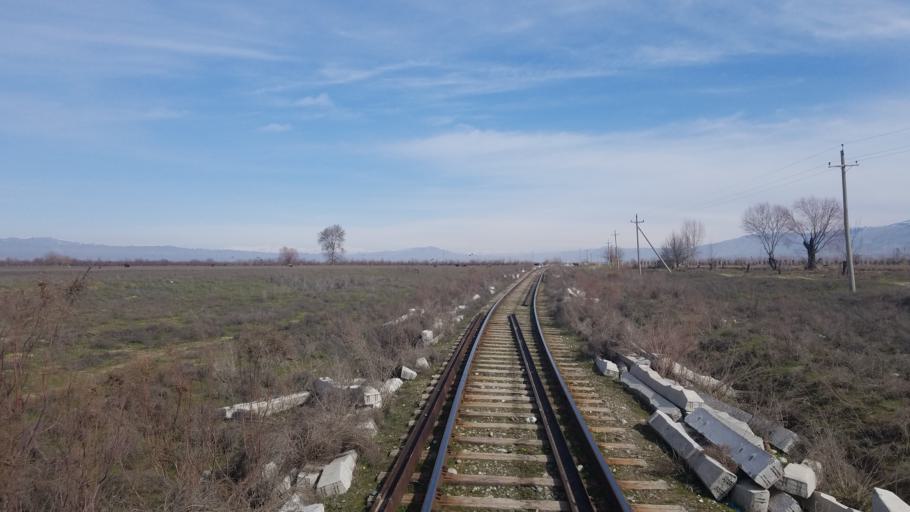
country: TJ
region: Khatlon
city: Abdurahmoni Jomi
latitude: 38.0429
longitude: 68.8496
